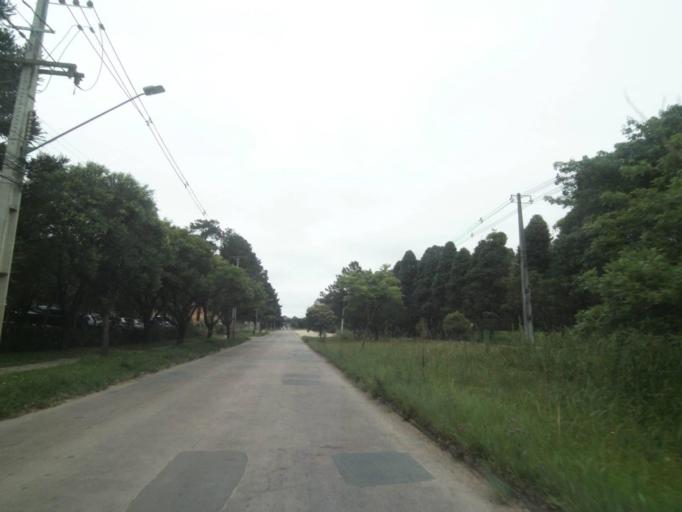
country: BR
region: Parana
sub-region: Araucaria
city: Araucaria
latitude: -25.5368
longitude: -49.3184
